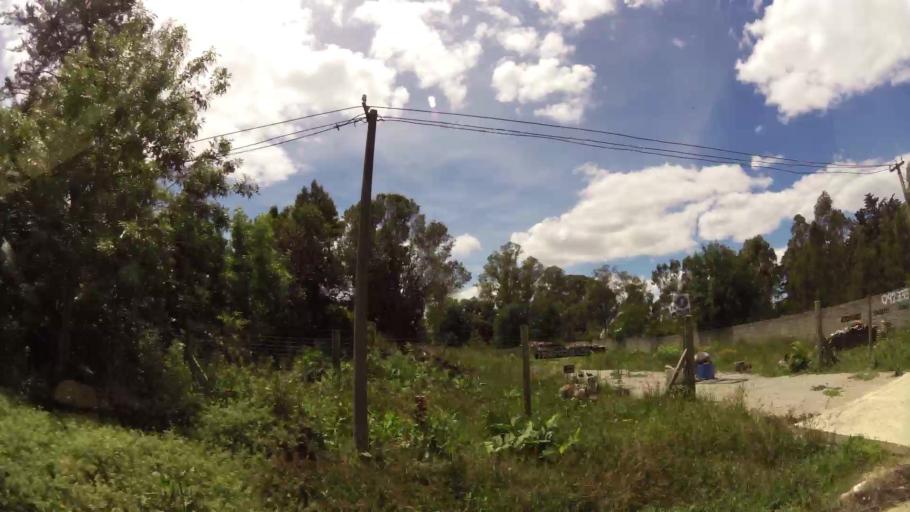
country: UY
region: Canelones
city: Colonia Nicolich
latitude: -34.8181
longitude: -55.9724
